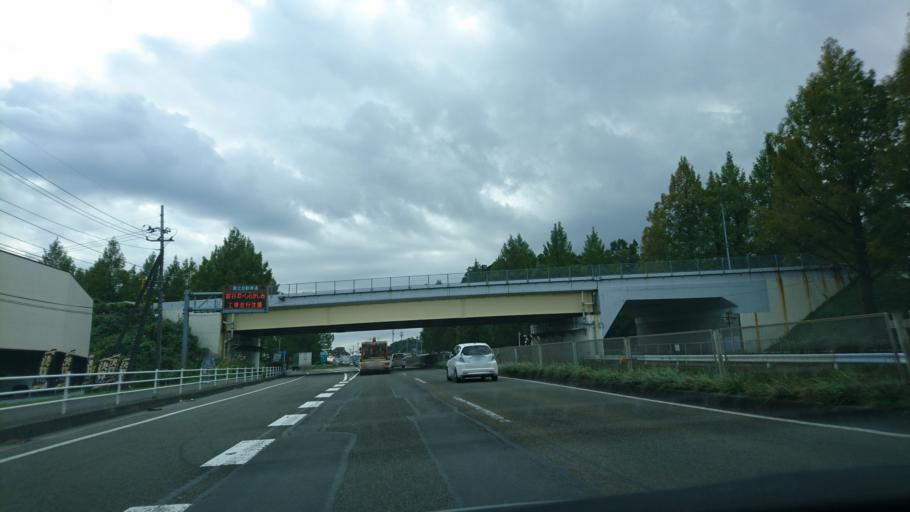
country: JP
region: Miyagi
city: Tomiya
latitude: 38.3448
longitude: 140.8792
